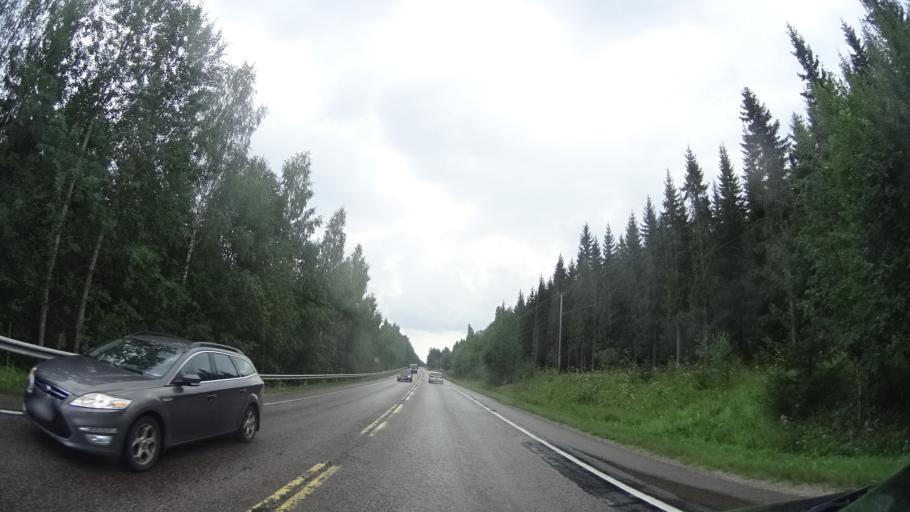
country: FI
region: Uusimaa
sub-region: Helsinki
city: Nurmijaervi
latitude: 60.4116
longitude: 24.7309
